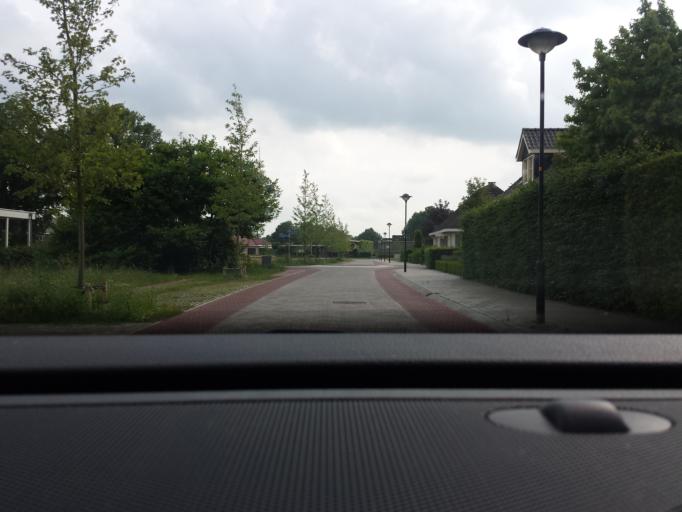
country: NL
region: Gelderland
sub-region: Gemeente Lochem
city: Barchem
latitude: 52.0833
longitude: 6.4631
